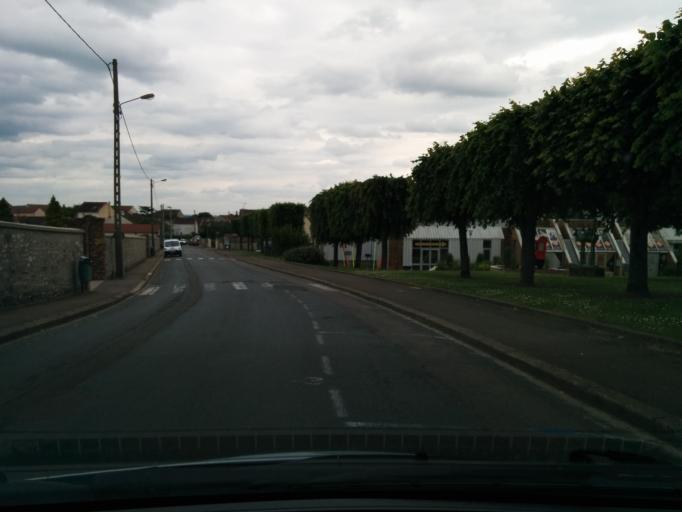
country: FR
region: Ile-de-France
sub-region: Departement des Yvelines
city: Mantes-la-Ville
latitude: 48.9763
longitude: 1.7080
